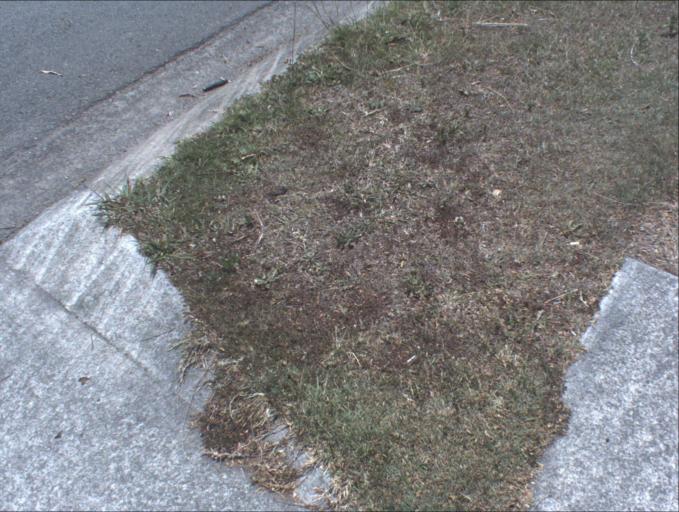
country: AU
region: Queensland
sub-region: Logan
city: Slacks Creek
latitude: -27.6678
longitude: 153.1475
